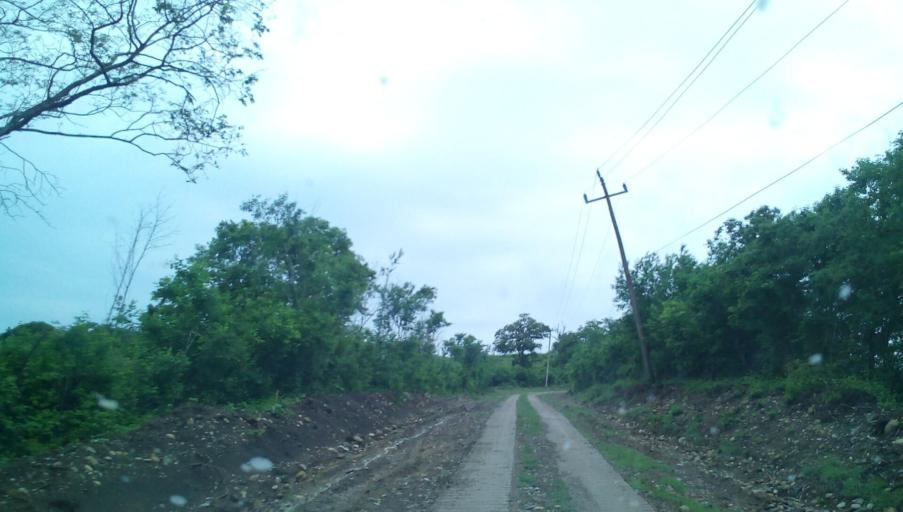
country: MX
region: Veracruz
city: Tempoal de Sanchez
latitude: 21.4517
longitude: -98.4256
